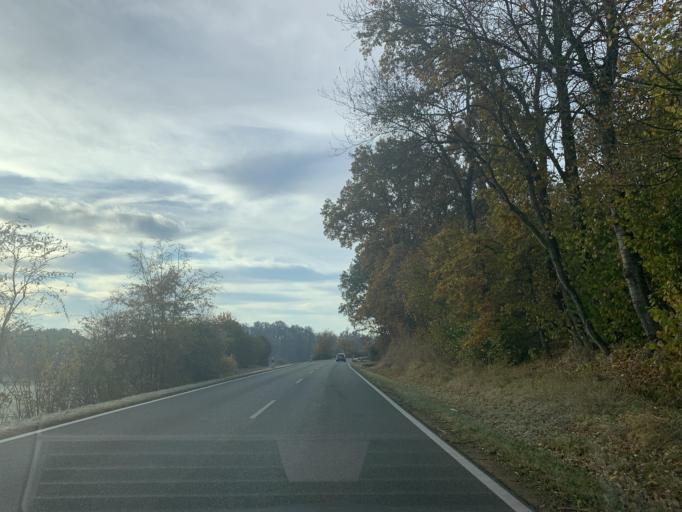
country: DE
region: Bavaria
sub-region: Upper Palatinate
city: Neunburg vorm Wald
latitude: 49.3667
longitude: 12.3784
